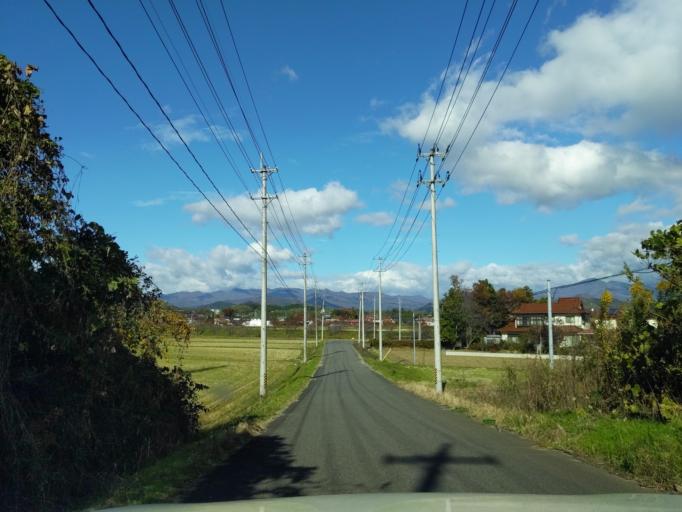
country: JP
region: Fukushima
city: Koriyama
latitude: 37.4501
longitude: 140.3216
